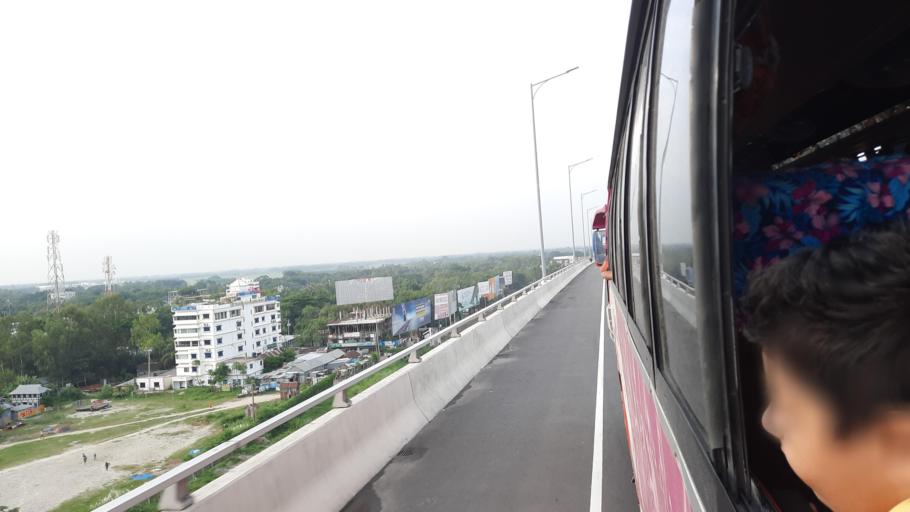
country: BD
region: Dhaka
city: Char Bhadrasan
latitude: 23.4715
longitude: 90.2647
